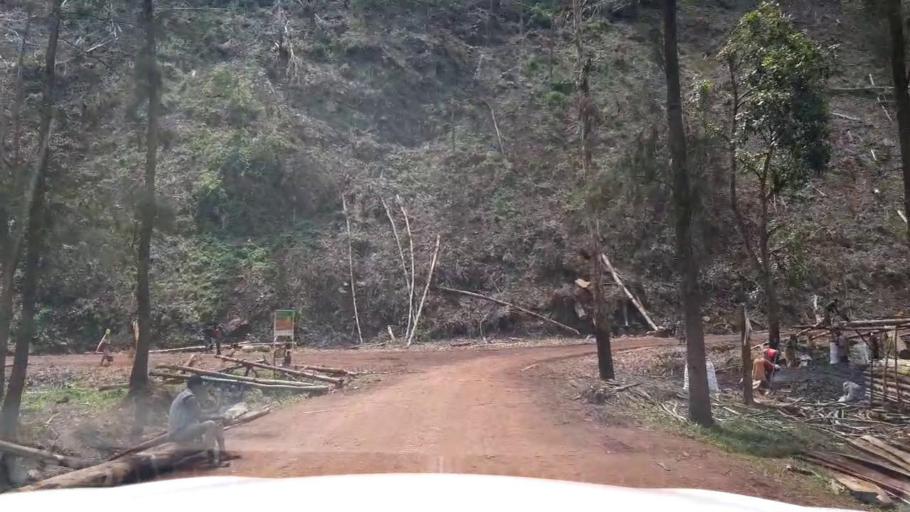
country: UG
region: Western Region
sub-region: Kisoro District
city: Kisoro
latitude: -1.3838
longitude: 29.7998
